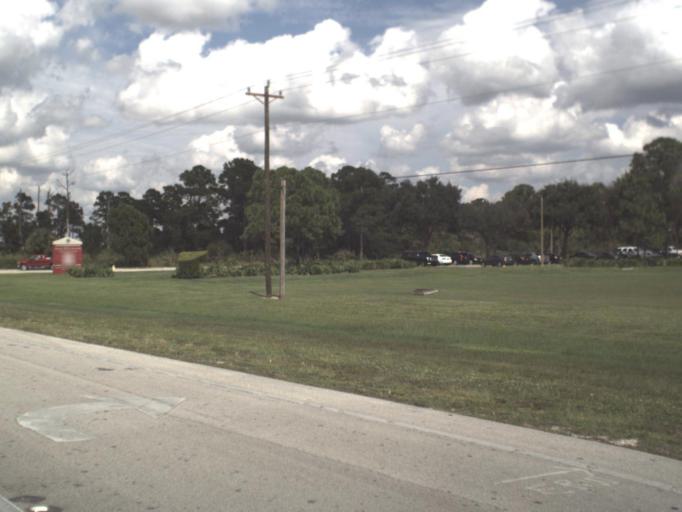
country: US
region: Florida
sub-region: Collier County
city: Immokalee
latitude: 26.4440
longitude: -81.4340
